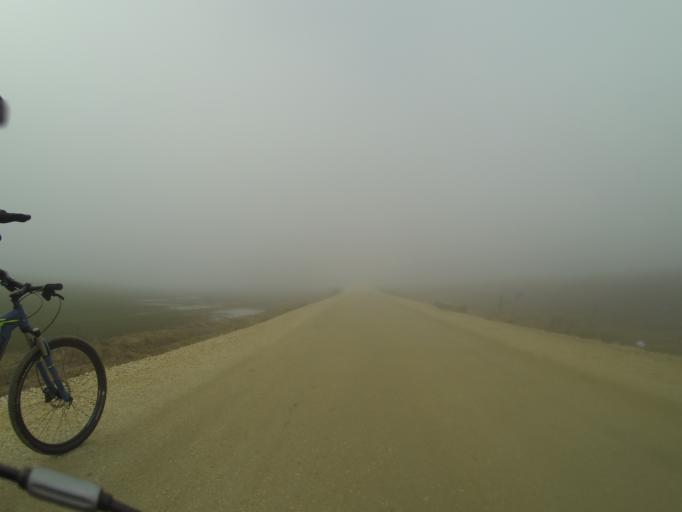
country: RO
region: Mehedinti
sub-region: Comuna Baclesu
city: Baclesu
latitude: 44.4423
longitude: 23.1307
